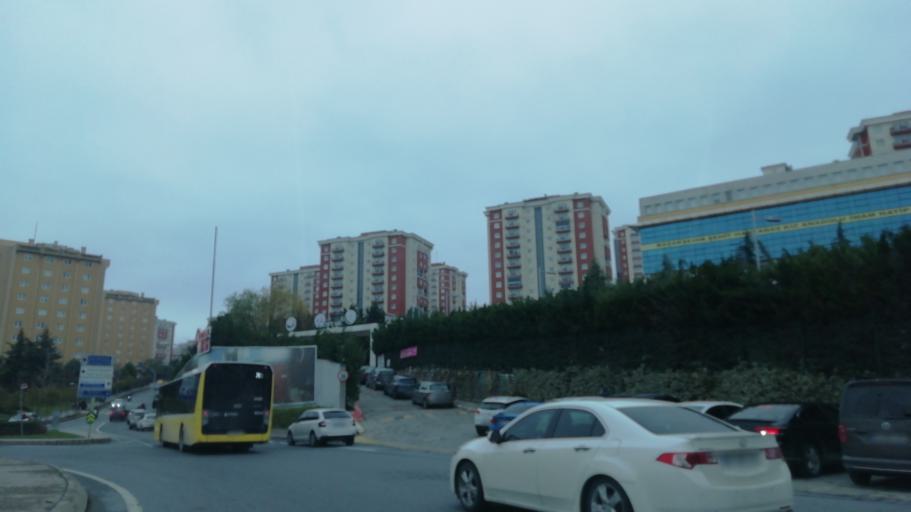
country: TR
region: Istanbul
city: Basaksehir
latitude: 41.0907
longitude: 28.8033
